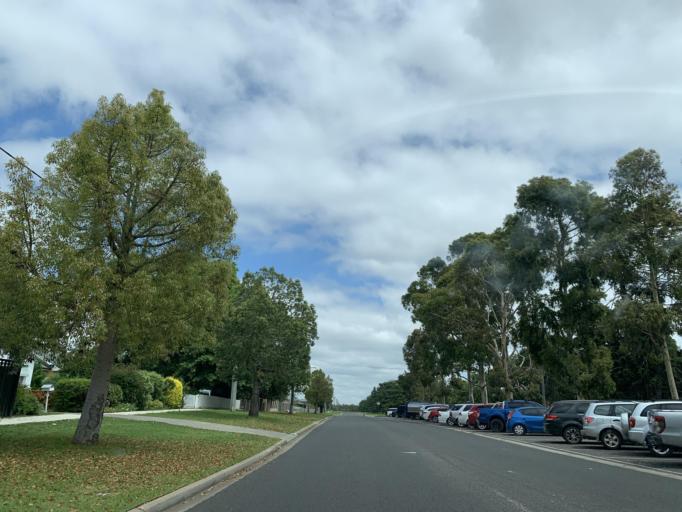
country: AU
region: Victoria
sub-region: Wellington
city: Sale
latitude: -38.1142
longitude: 147.0808
